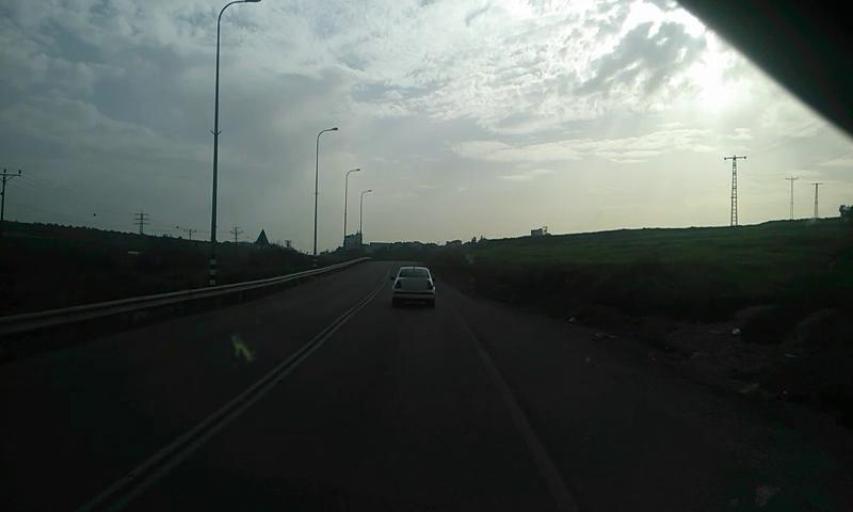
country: PS
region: West Bank
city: Hajjah
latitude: 32.1955
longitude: 35.1434
